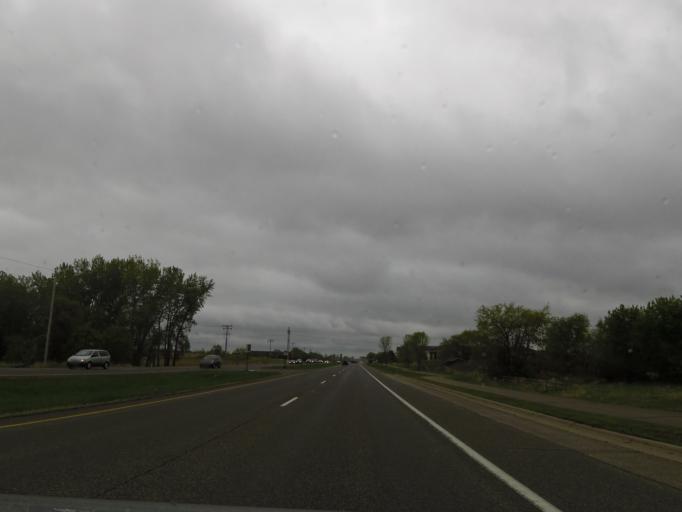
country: US
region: Minnesota
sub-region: Washington County
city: Oakdale
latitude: 44.9585
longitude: -92.9342
